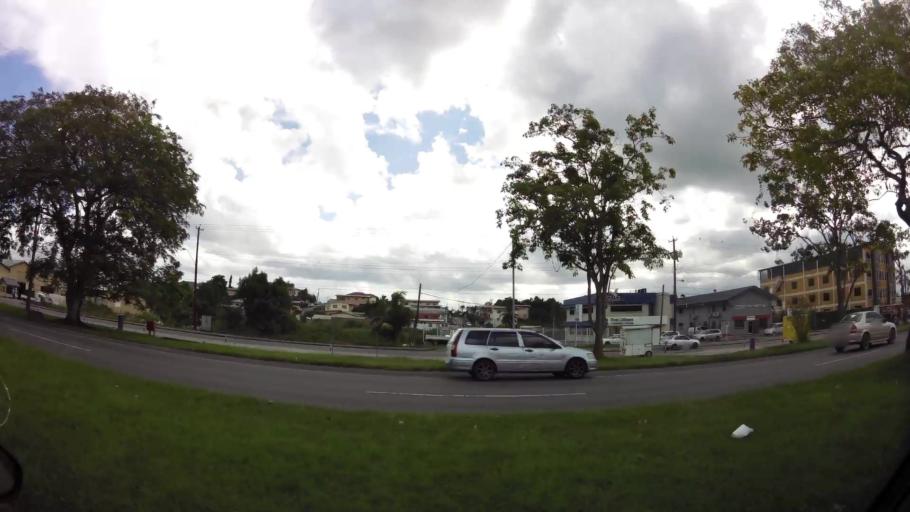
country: TT
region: City of San Fernando
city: San Fernando
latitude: 10.2662
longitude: -61.4618
